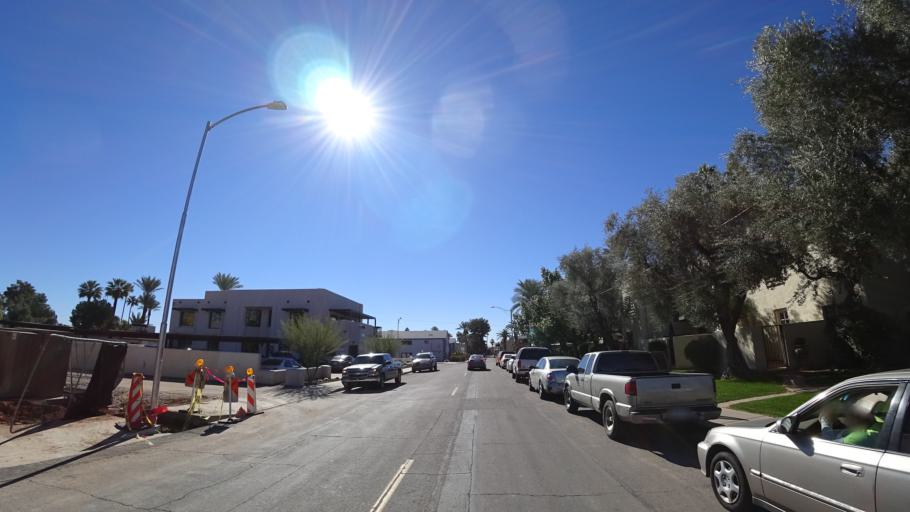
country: US
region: Arizona
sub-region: Maricopa County
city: Scottsdale
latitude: 33.4918
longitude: -111.9326
